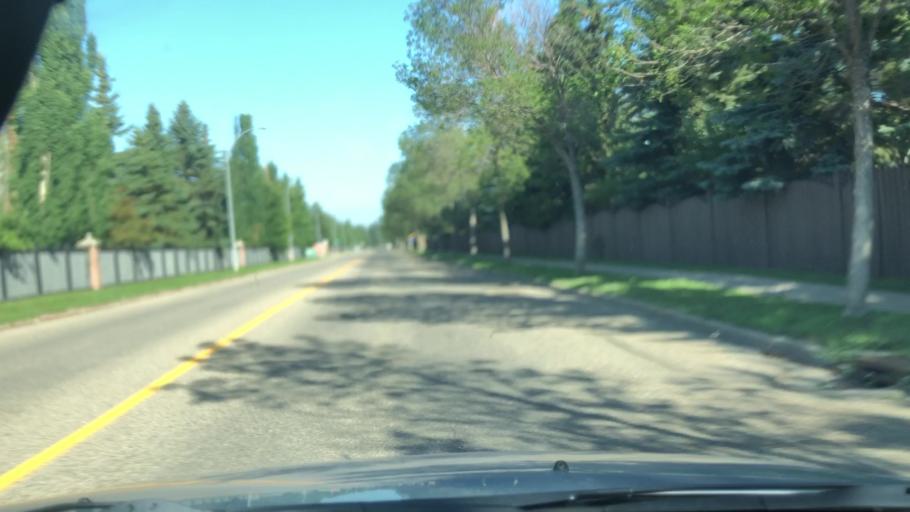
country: CA
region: Alberta
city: Edmonton
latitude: 53.4735
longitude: -113.5966
